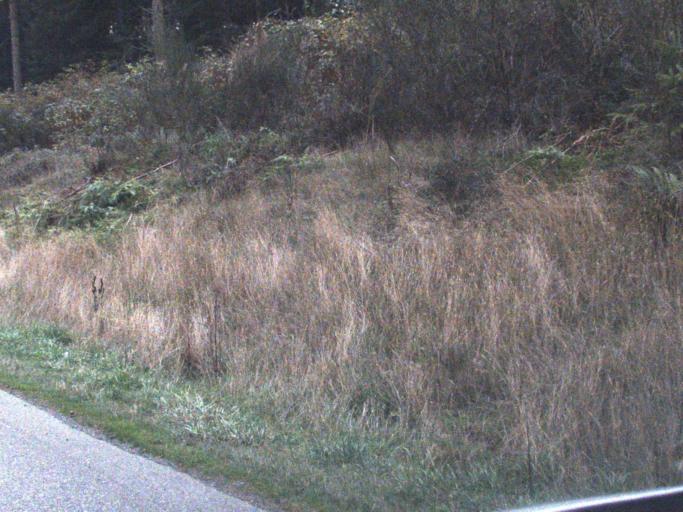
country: US
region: Washington
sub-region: Island County
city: Freeland
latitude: 48.0417
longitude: -122.5651
